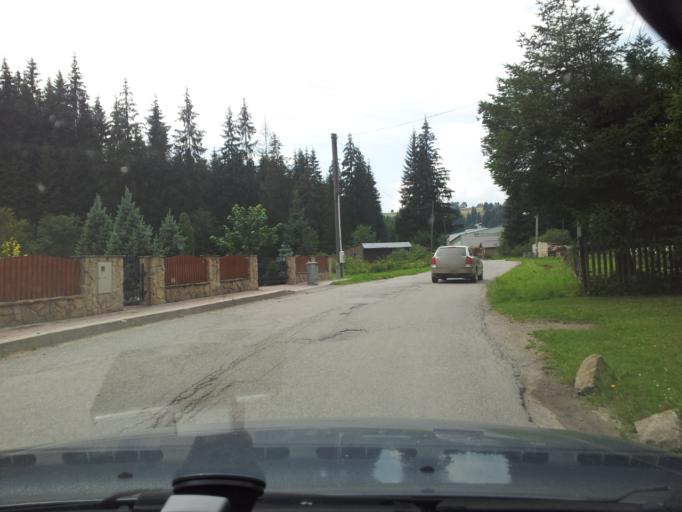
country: SK
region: Zilinsky
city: Oravska Lesna
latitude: 49.3639
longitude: 19.1802
